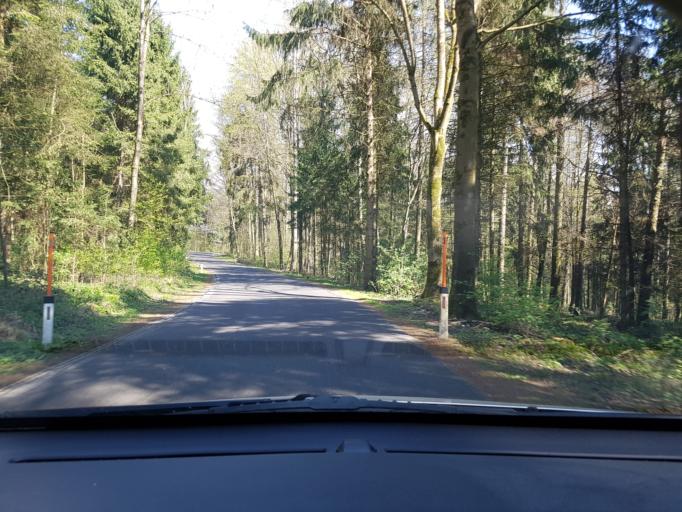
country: AT
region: Upper Austria
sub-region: Politischer Bezirk Linz-Land
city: Sankt Florian
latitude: 48.2057
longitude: 14.3392
